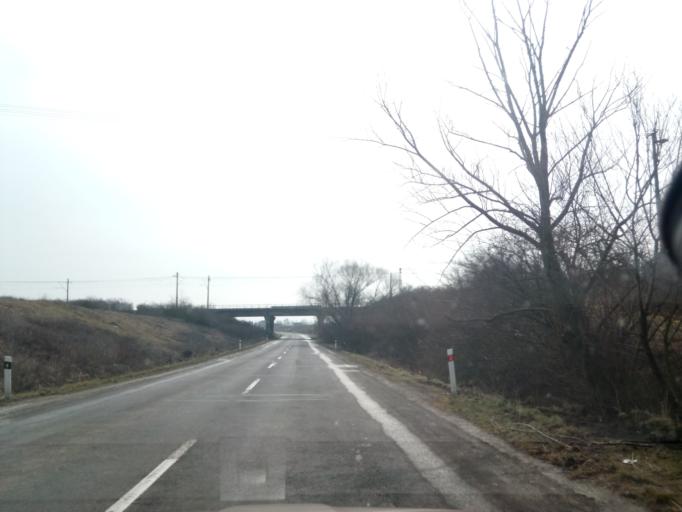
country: SK
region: Kosicky
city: Secovce
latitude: 48.6214
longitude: 21.5916
